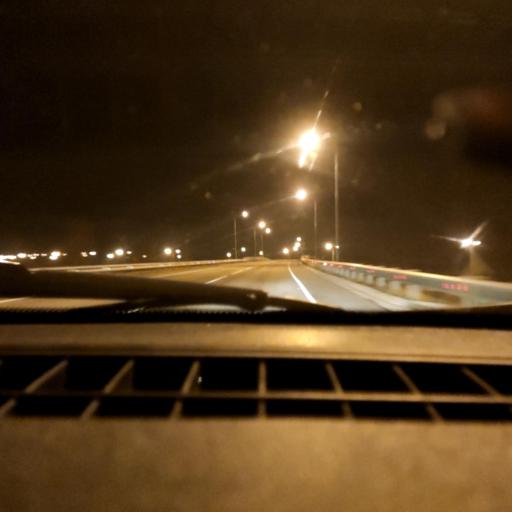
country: RU
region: Bashkortostan
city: Kushnarenkovo
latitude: 55.0604
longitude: 55.4257
